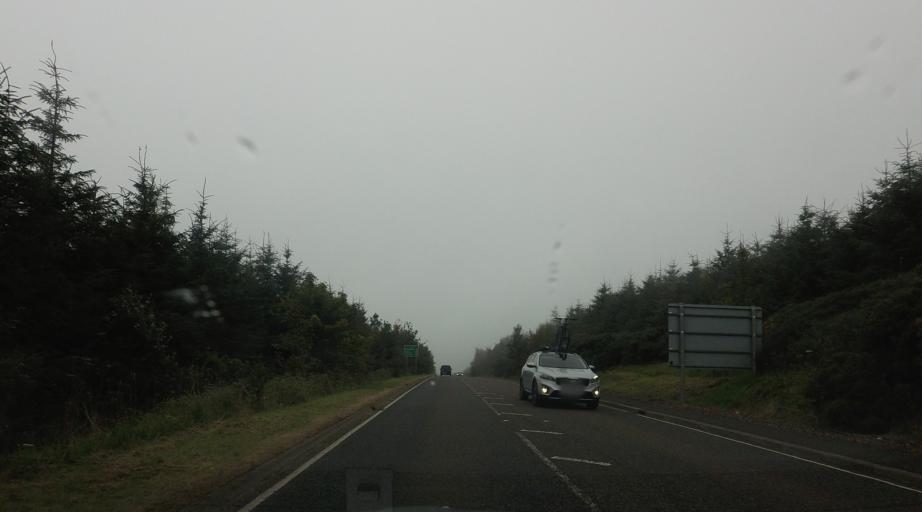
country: GB
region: Scotland
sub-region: Highland
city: Thurso
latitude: 58.2458
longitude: -3.4417
